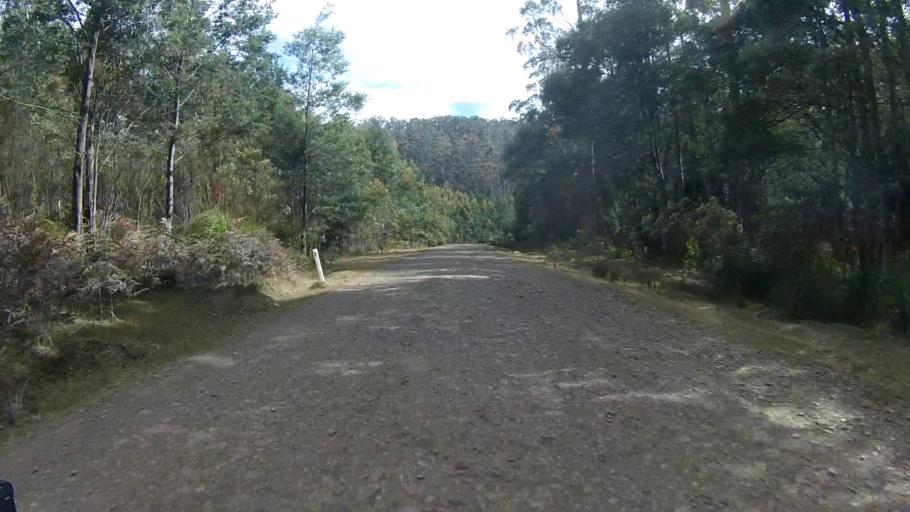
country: AU
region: Tasmania
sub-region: Sorell
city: Sorell
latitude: -42.7424
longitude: 147.8284
